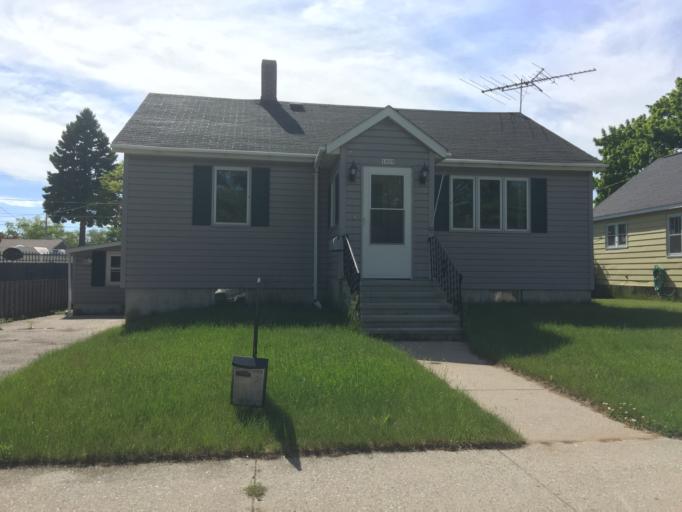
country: US
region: Michigan
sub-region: Menominee County
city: Menominee
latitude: 45.1156
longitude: -87.6237
